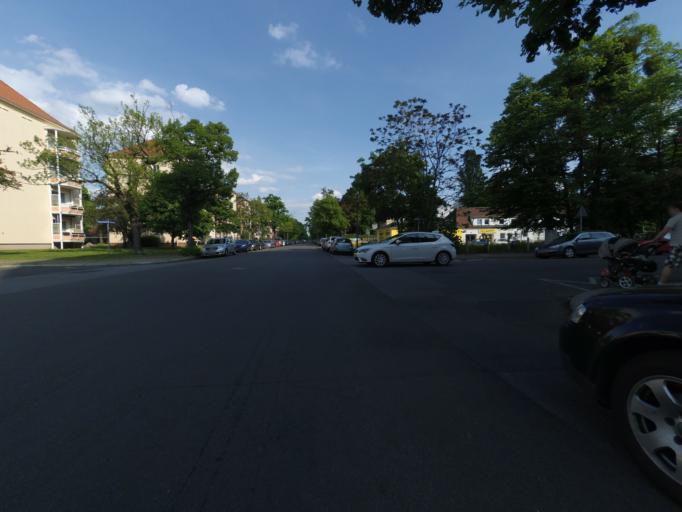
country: DE
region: Saxony
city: Dresden
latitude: 51.0409
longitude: 13.7717
